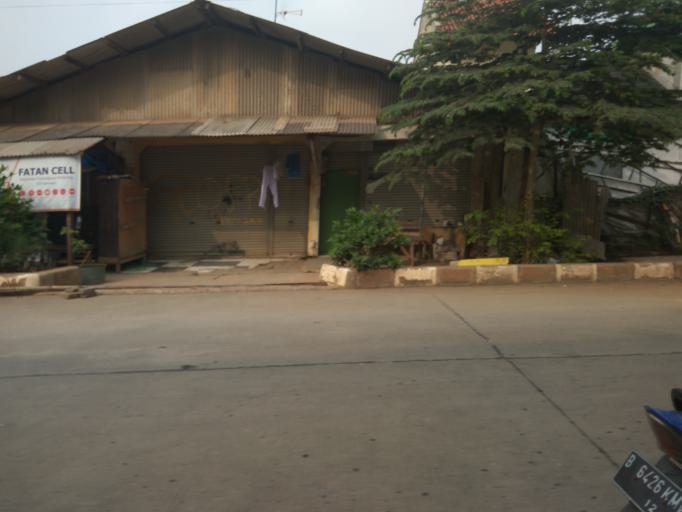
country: ID
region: West Java
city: Bekasi
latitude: -6.2497
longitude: 106.9372
